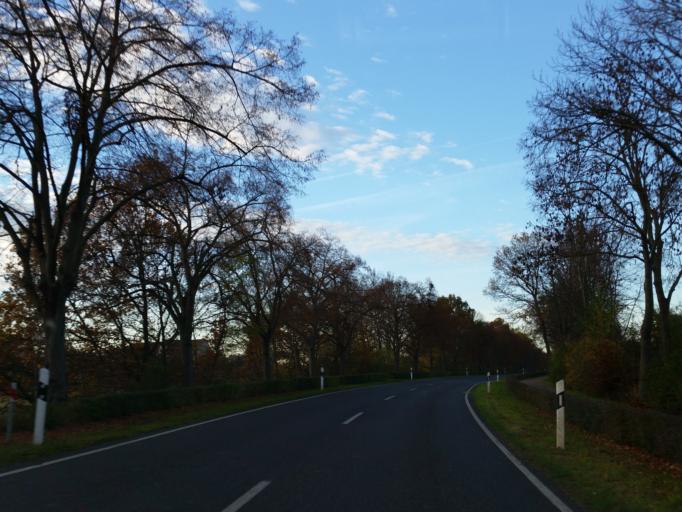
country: DE
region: Lower Saxony
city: Braunschweig
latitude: 52.2653
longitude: 10.5829
